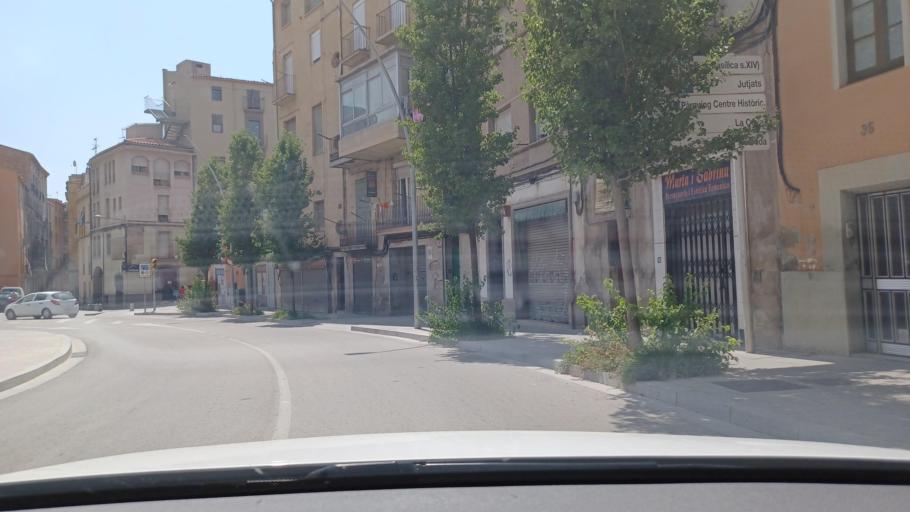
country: ES
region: Catalonia
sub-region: Provincia de Barcelona
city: Manresa
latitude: 41.7249
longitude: 1.8293
